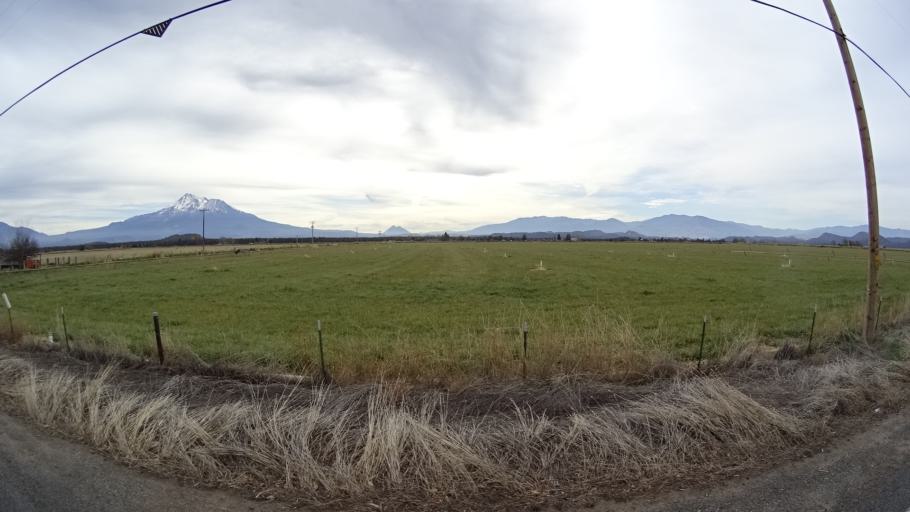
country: US
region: California
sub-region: Siskiyou County
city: Montague
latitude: 41.6239
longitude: -122.3904
